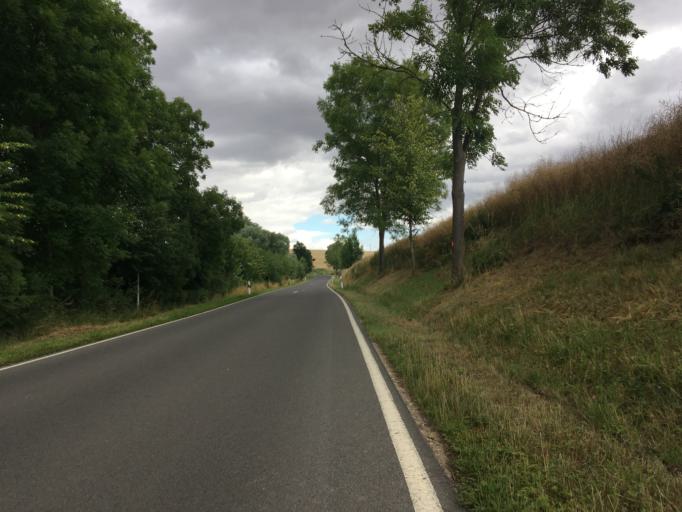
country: DE
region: Brandenburg
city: Gramzow
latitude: 53.2307
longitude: 13.9434
